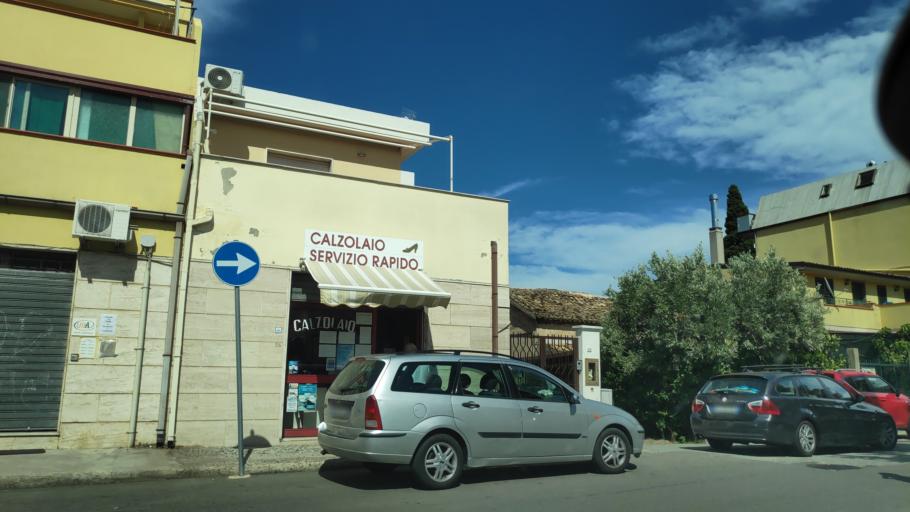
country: IT
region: Calabria
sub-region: Provincia di Catanzaro
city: Montepaone Lido
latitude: 38.7290
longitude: 16.5405
